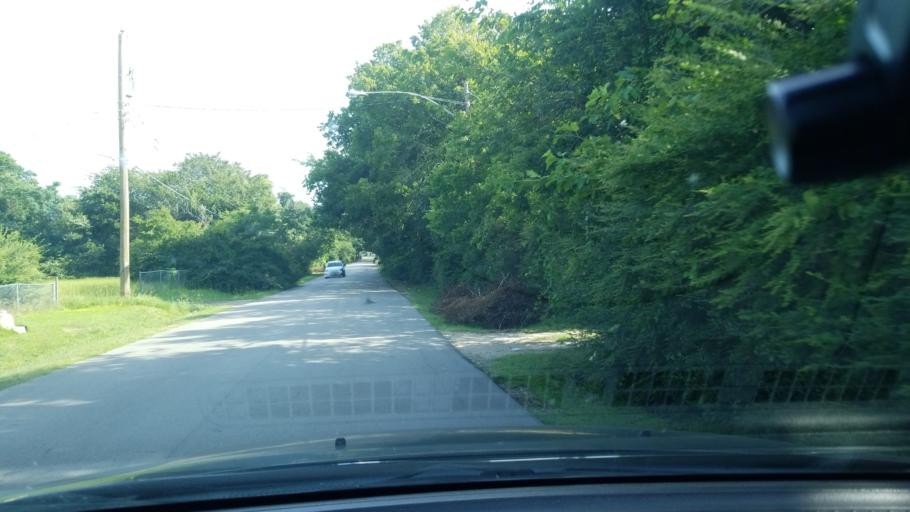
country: US
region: Texas
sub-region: Dallas County
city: Balch Springs
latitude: 32.7200
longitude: -96.6455
